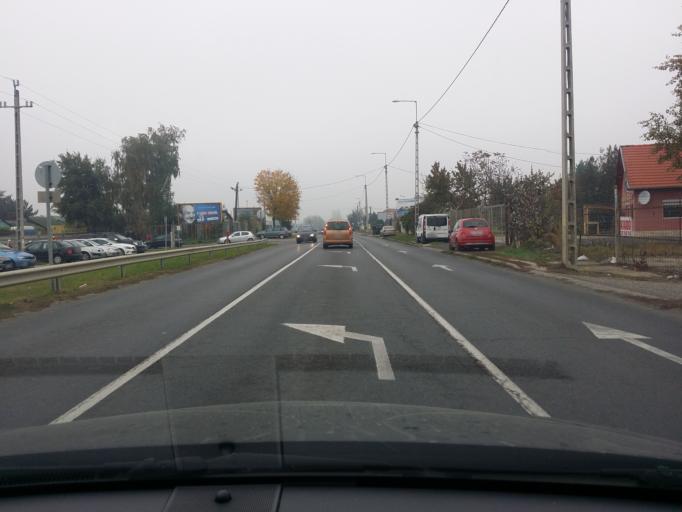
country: HU
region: Szabolcs-Szatmar-Bereg
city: Nyiregyhaza
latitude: 47.9697
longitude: 21.6946
